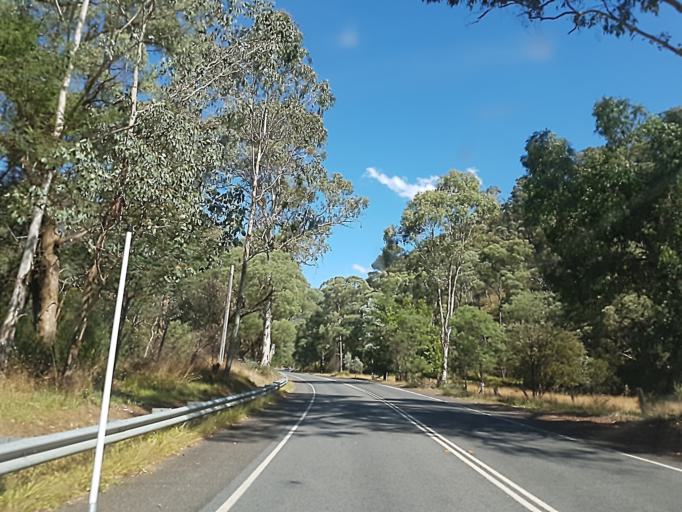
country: AU
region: Victoria
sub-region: Alpine
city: Mount Beauty
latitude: -36.8455
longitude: 147.0780
